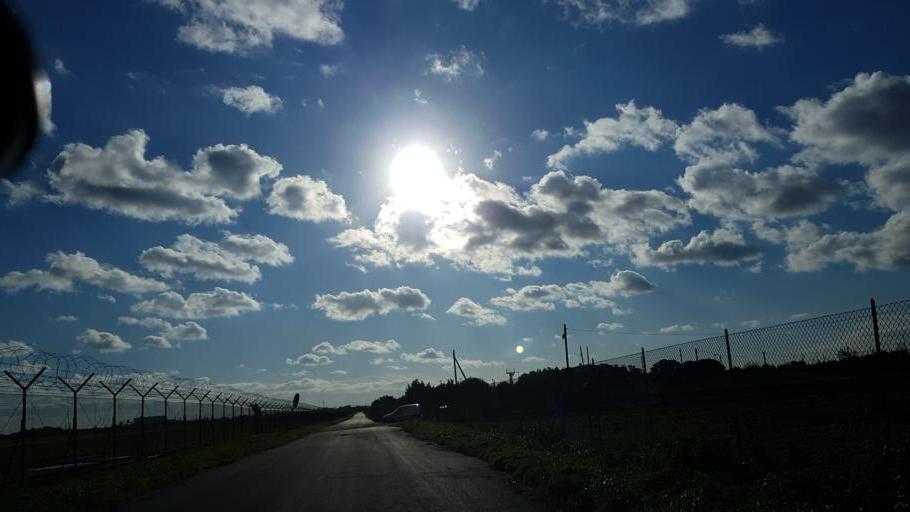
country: IT
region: Apulia
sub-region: Provincia di Brindisi
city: Materdomini
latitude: 40.6648
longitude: 17.9361
